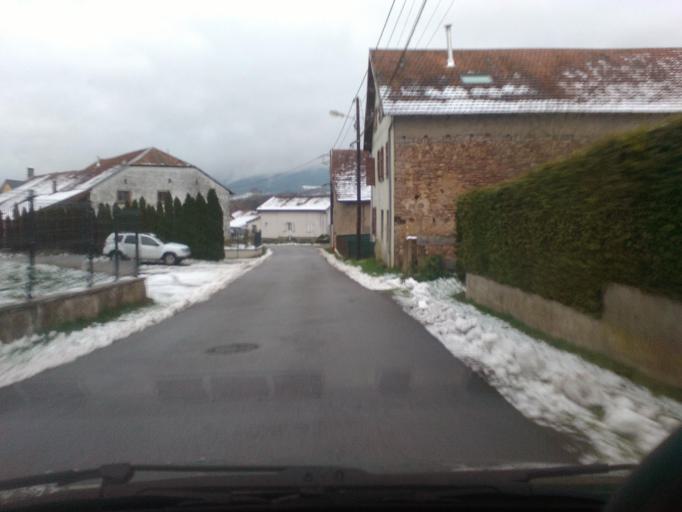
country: FR
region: Lorraine
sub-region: Departement des Vosges
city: Ban-de-Laveline
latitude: 48.2787
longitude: 7.0348
